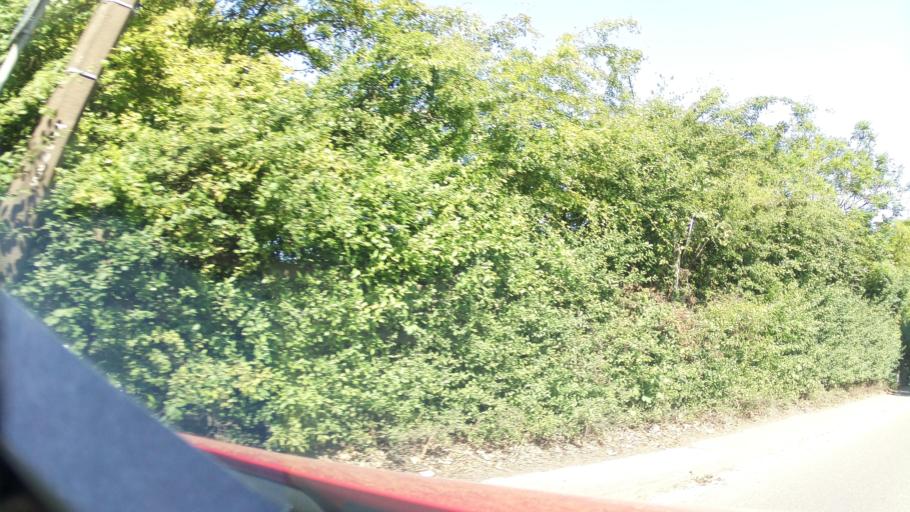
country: GB
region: England
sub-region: Derbyshire
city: Belper
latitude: 53.0180
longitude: -1.4847
